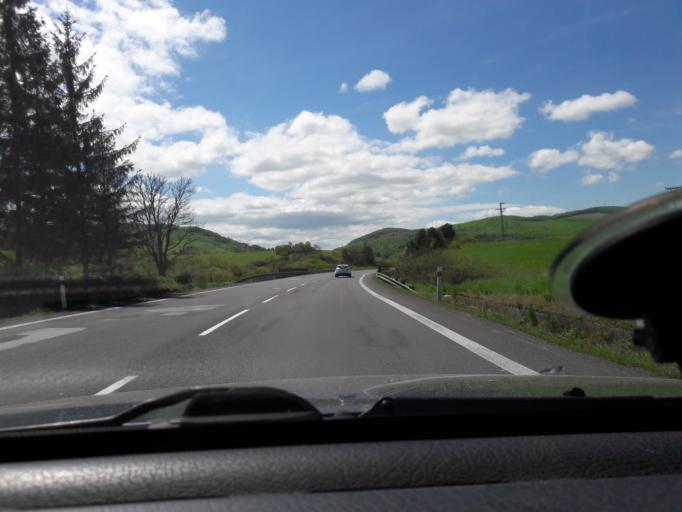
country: SK
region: Banskobystricky
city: Krupina
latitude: 48.4304
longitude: 19.0951
